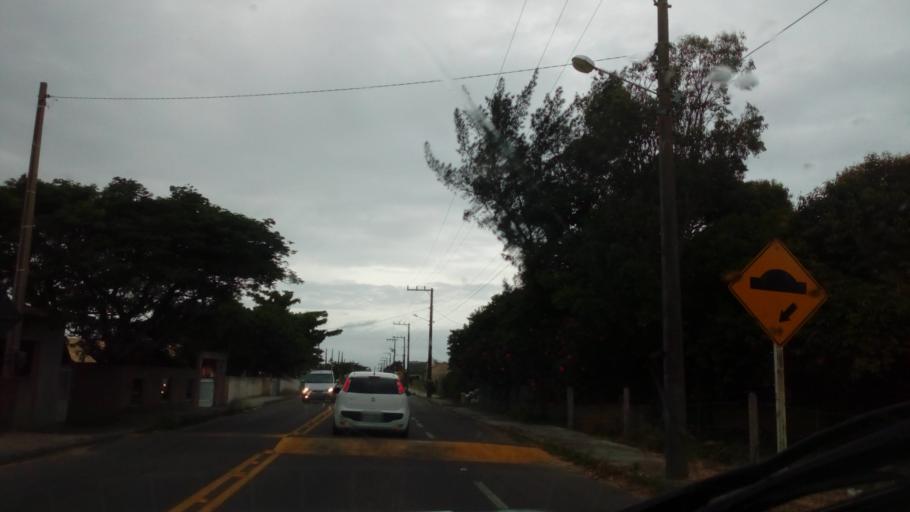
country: BR
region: Santa Catarina
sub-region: Laguna
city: Laguna
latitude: -28.5780
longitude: -48.8243
